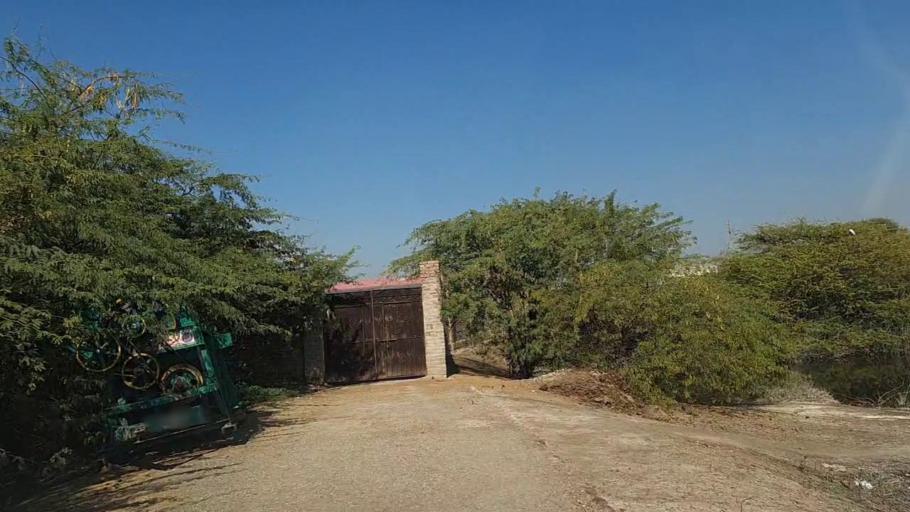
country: PK
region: Sindh
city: Nawabshah
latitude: 26.3413
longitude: 68.3544
